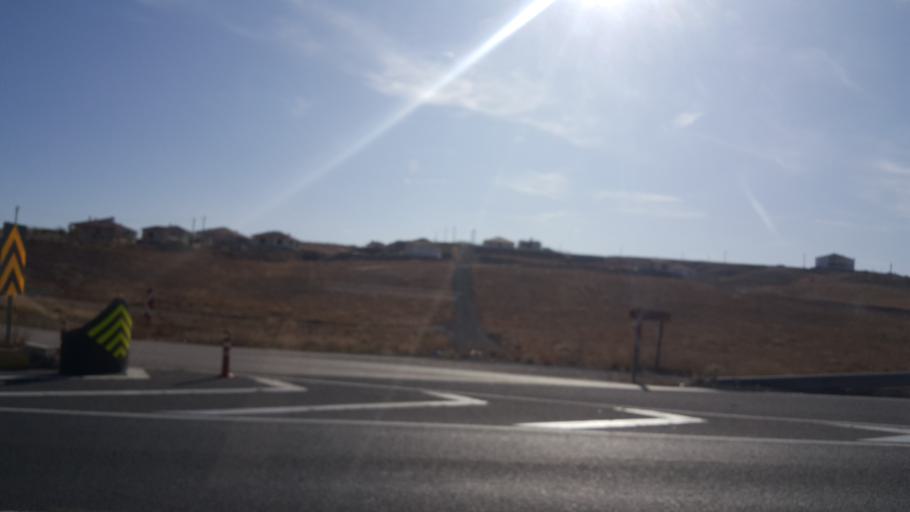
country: TR
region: Konya
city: Kulu
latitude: 39.2709
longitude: 32.9659
